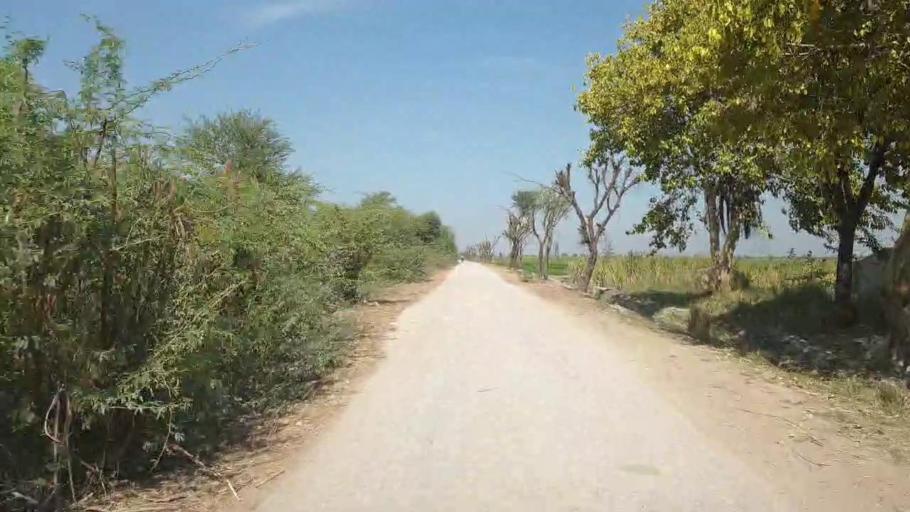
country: PK
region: Sindh
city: Mirwah Gorchani
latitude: 25.4285
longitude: 69.1662
